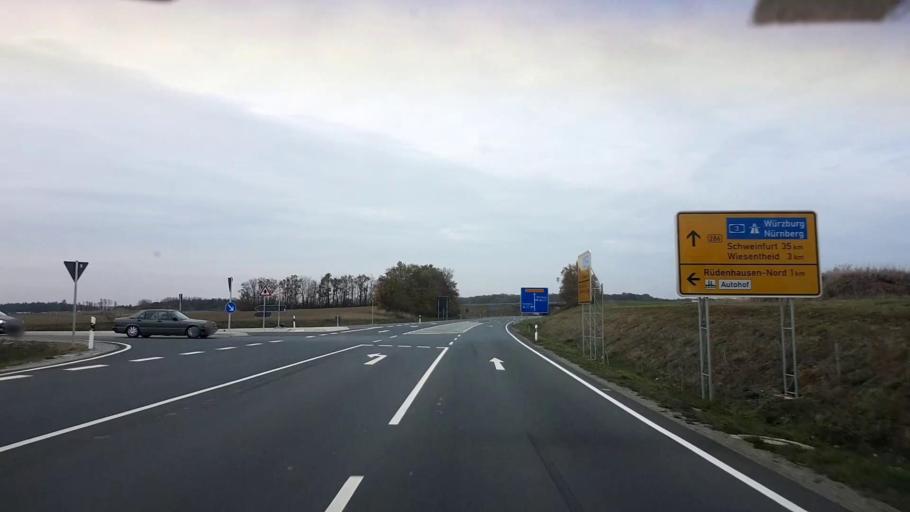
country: DE
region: Bavaria
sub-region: Regierungsbezirk Unterfranken
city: Castell
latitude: 49.7716
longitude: 10.3460
